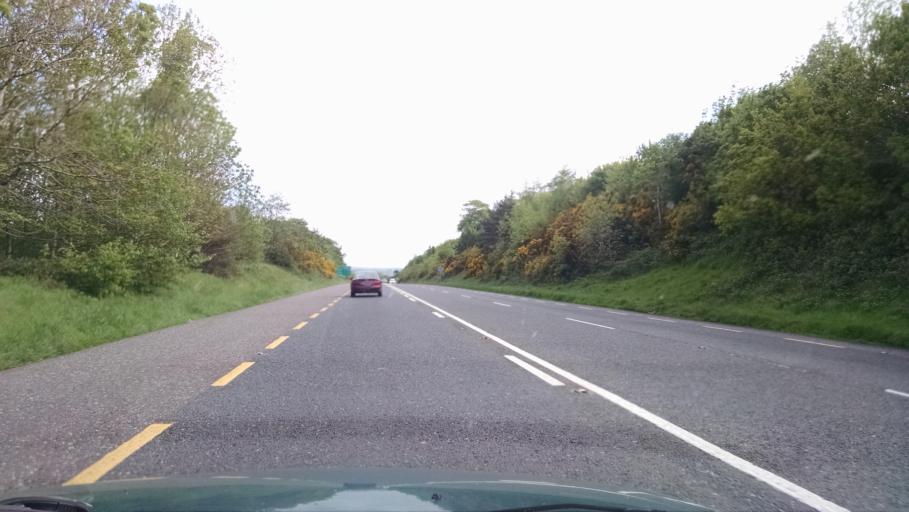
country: IE
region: Munster
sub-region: County Cork
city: Carrigaline
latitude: 51.8622
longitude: -8.4194
